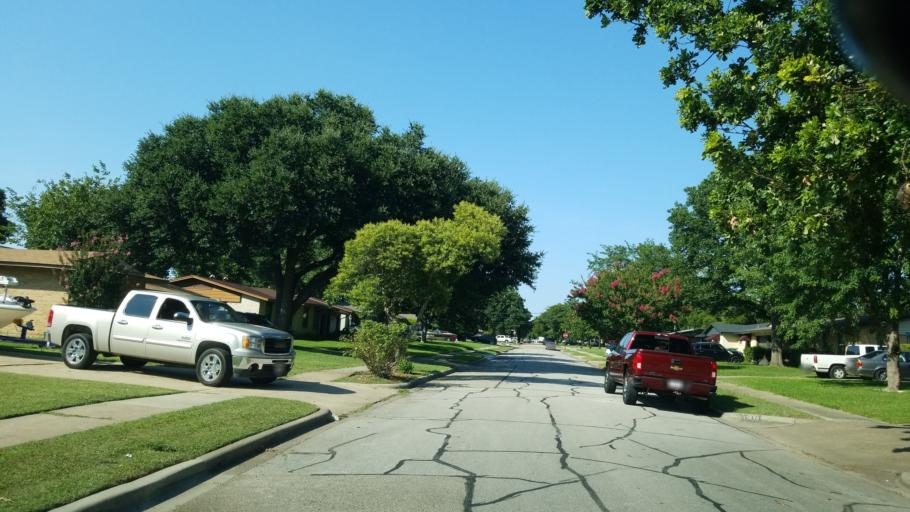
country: US
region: Texas
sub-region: Dallas County
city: Farmers Branch
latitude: 32.9305
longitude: -96.8862
